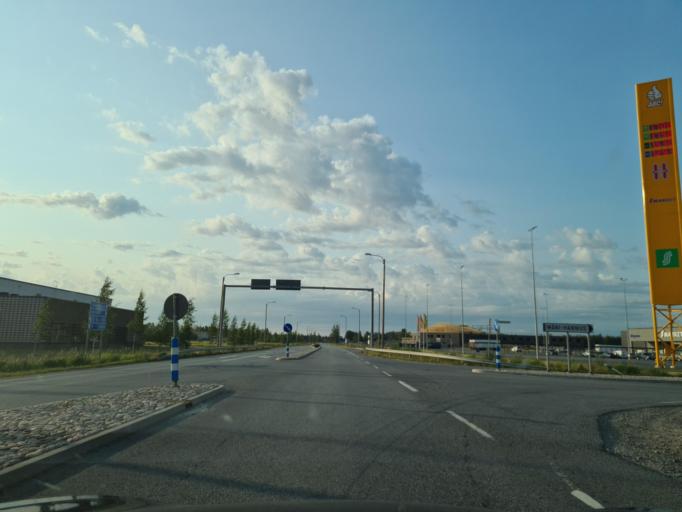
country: FI
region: Southern Ostrobothnia
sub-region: Seinaejoki
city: Kauhava
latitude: 63.0895
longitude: 23.0585
